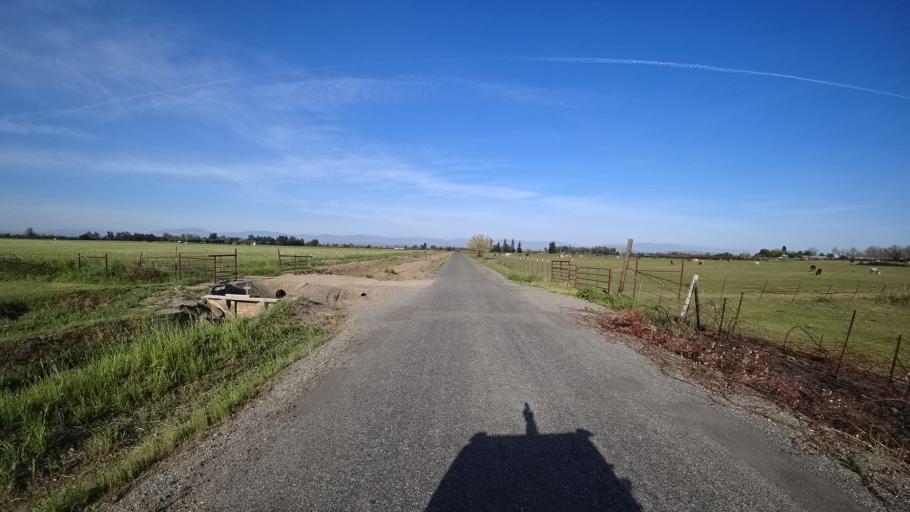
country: US
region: California
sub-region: Glenn County
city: Orland
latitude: 39.7151
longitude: -122.2301
